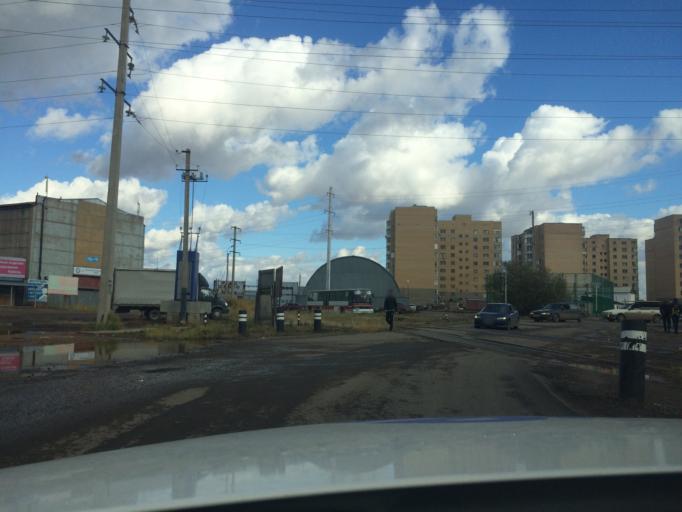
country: KZ
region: Astana Qalasy
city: Astana
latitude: 51.1840
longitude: 71.4352
